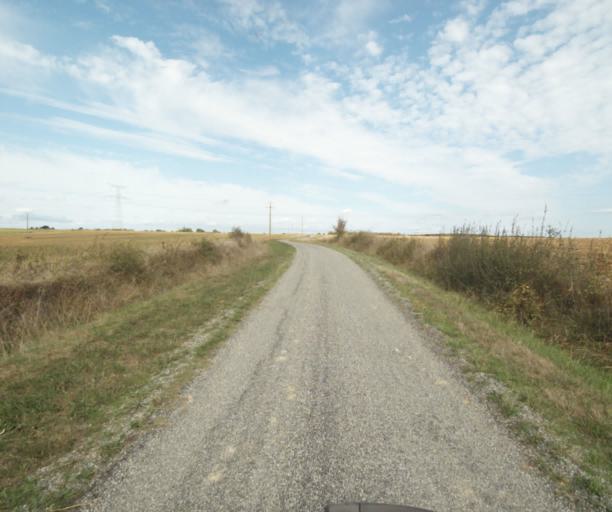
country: FR
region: Midi-Pyrenees
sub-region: Departement du Tarn-et-Garonne
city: Verdun-sur-Garonne
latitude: 43.8655
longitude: 1.1787
